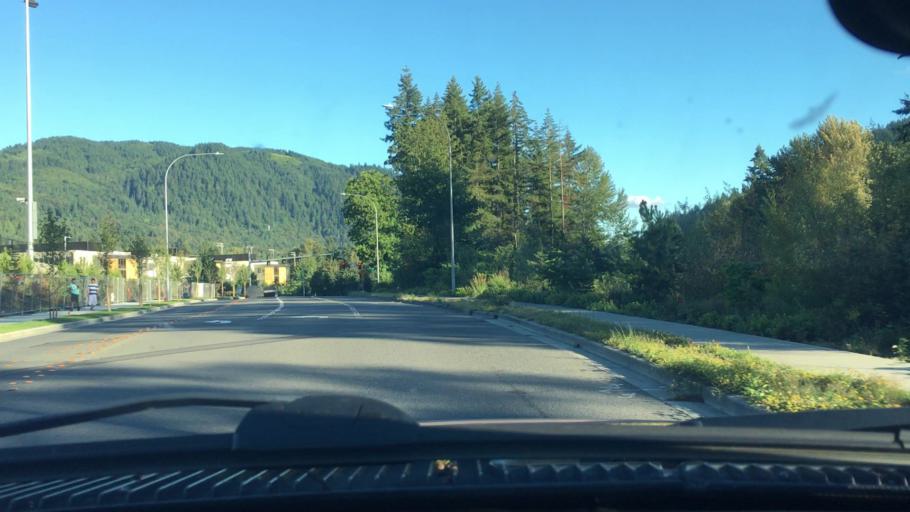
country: US
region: Washington
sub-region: King County
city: Issaquah
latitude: 47.5243
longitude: -122.0318
